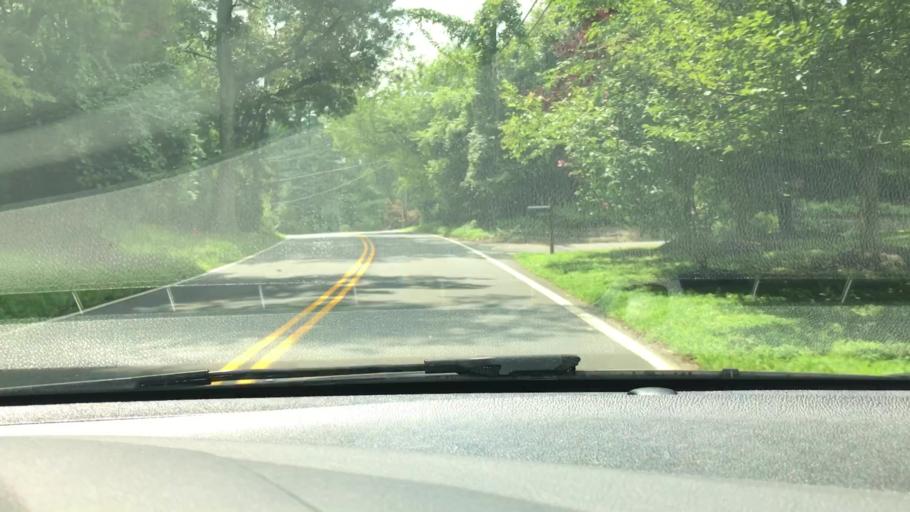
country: US
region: Maryland
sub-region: Montgomery County
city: Brookmont
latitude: 38.9316
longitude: -77.1435
